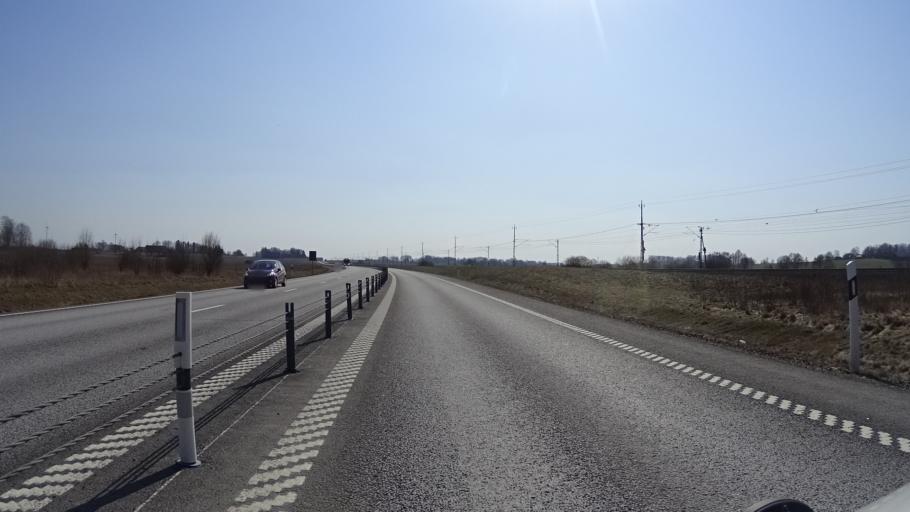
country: SE
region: OEstergoetland
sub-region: Motala Kommun
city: Stenstorp
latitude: 58.4948
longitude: 15.0268
